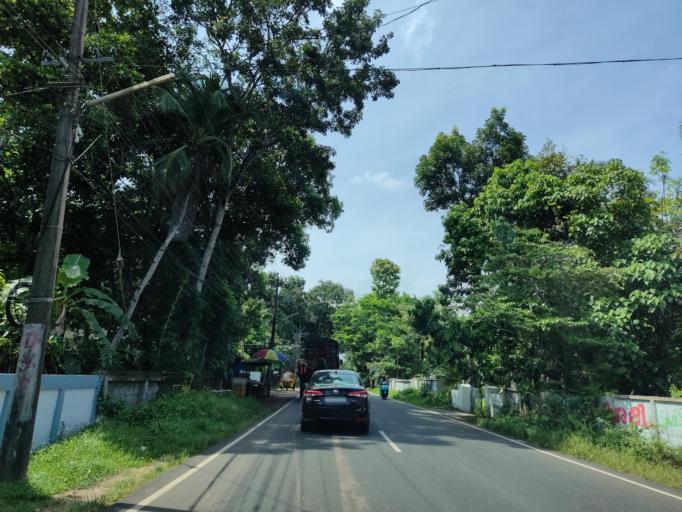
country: IN
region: Kerala
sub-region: Alappuzha
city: Mavelikara
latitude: 9.2940
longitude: 76.5330
